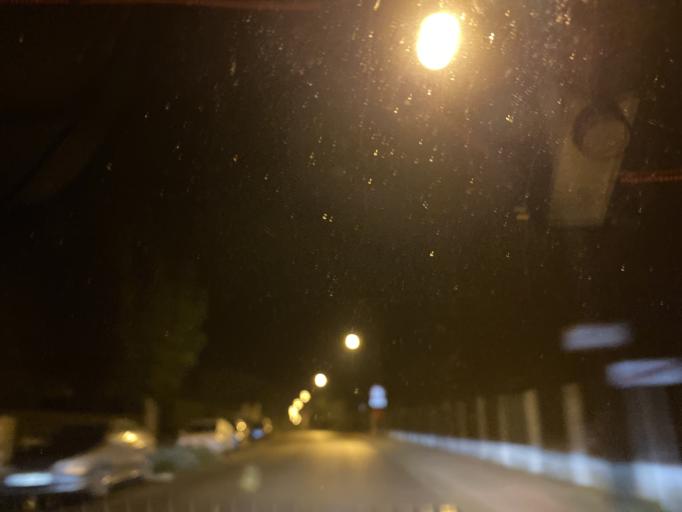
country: FR
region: Auvergne
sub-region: Departement de l'Allier
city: Abrest
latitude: 46.1131
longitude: 3.4379
